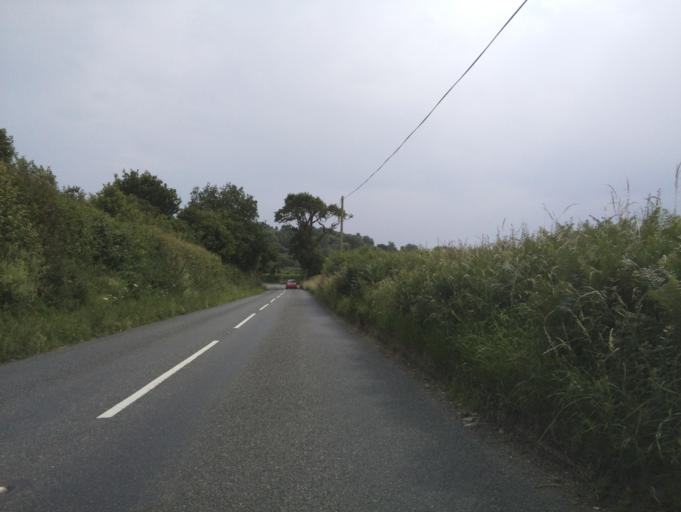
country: GB
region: England
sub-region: Devon
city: Colyton
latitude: 50.7182
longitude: -3.0524
